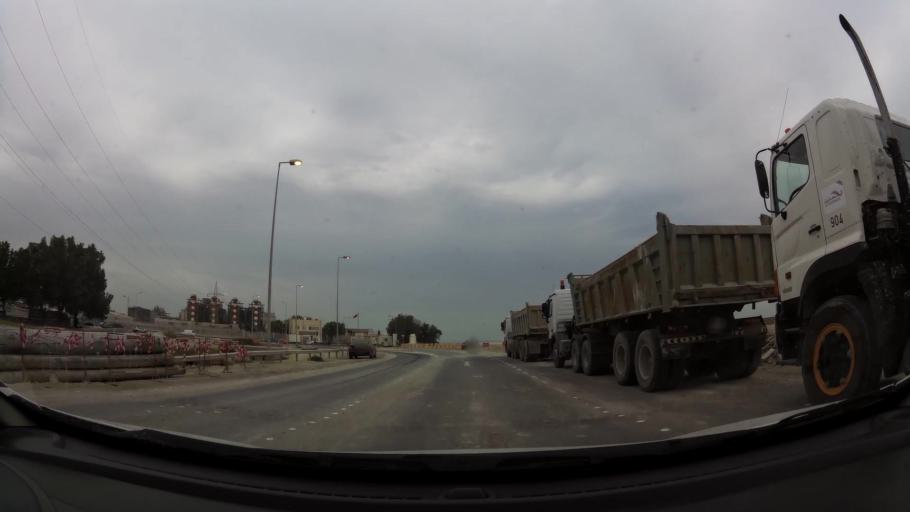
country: BH
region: Northern
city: Sitrah
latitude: 26.1799
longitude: 50.6229
